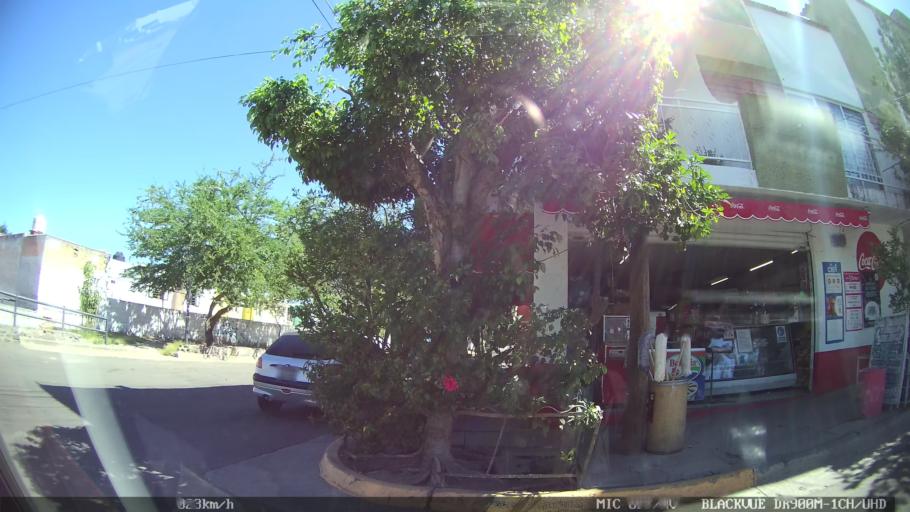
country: MX
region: Jalisco
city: Tlaquepaque
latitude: 20.6973
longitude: -103.2835
